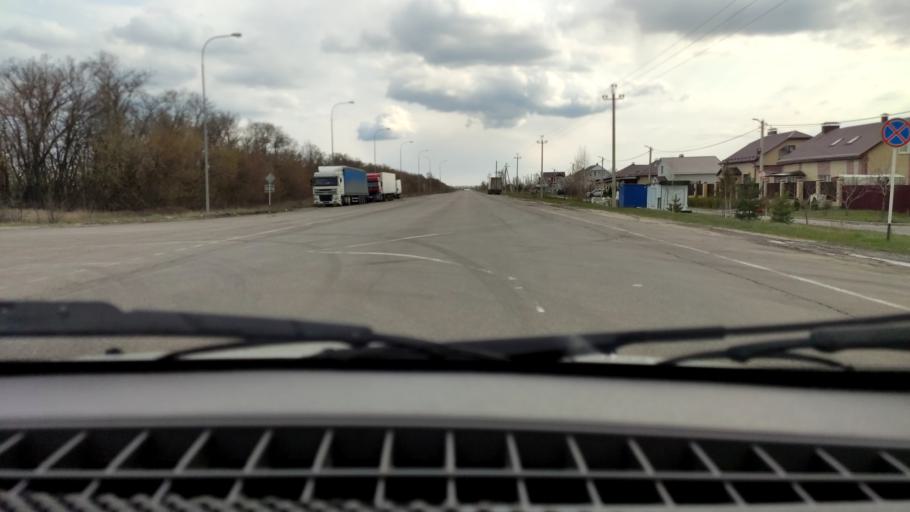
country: RU
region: Voronezj
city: Novaya Usman'
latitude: 51.6208
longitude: 39.3354
